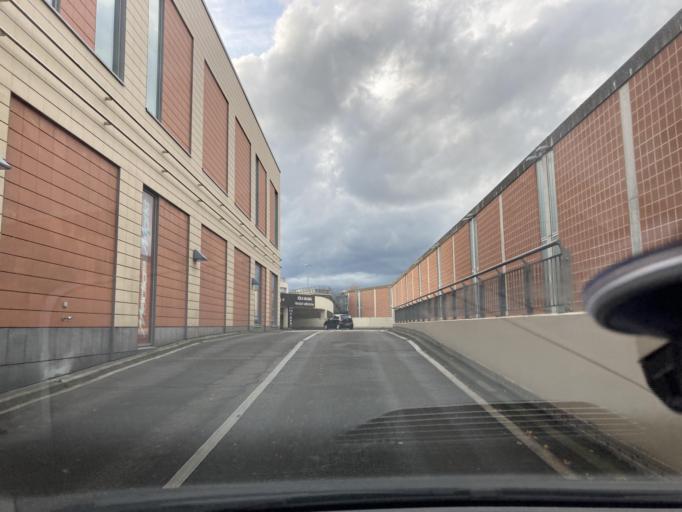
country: DE
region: North Rhine-Westphalia
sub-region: Regierungsbezirk Koln
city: Kalk
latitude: 50.9392
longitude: 6.9989
